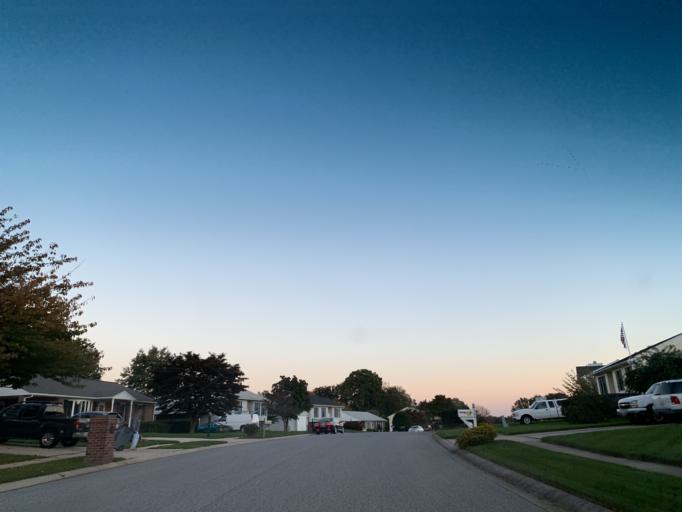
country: US
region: Maryland
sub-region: Harford County
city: South Bel Air
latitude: 39.5447
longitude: -76.3033
